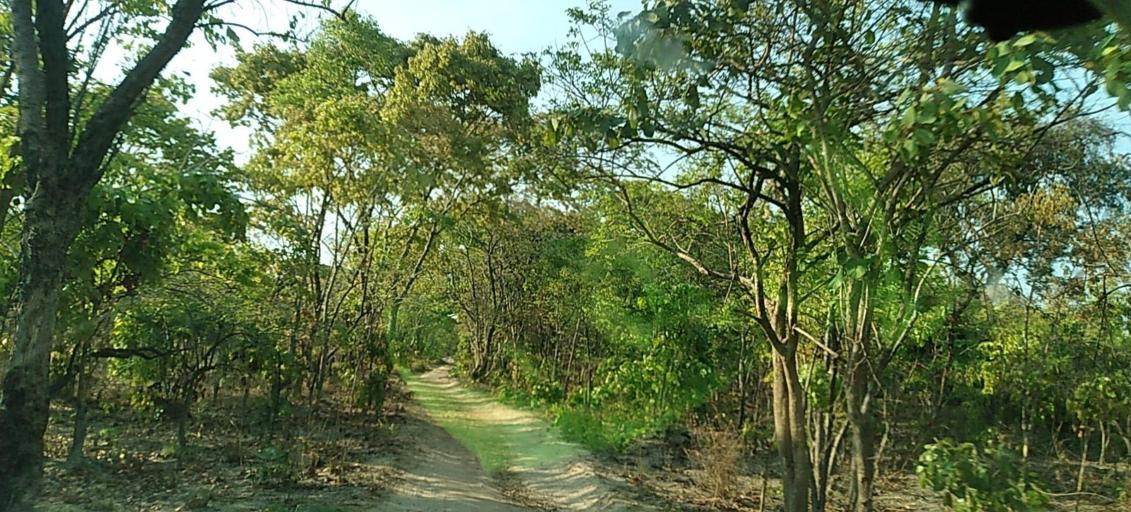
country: ZM
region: North-Western
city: Kalengwa
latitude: -13.1704
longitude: 25.0365
